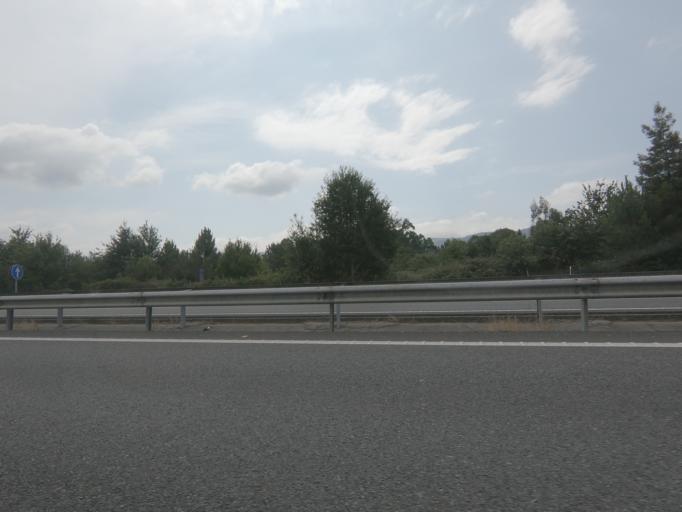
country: ES
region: Galicia
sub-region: Provincia de Pontevedra
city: Porrino
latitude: 42.1472
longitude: -8.6254
